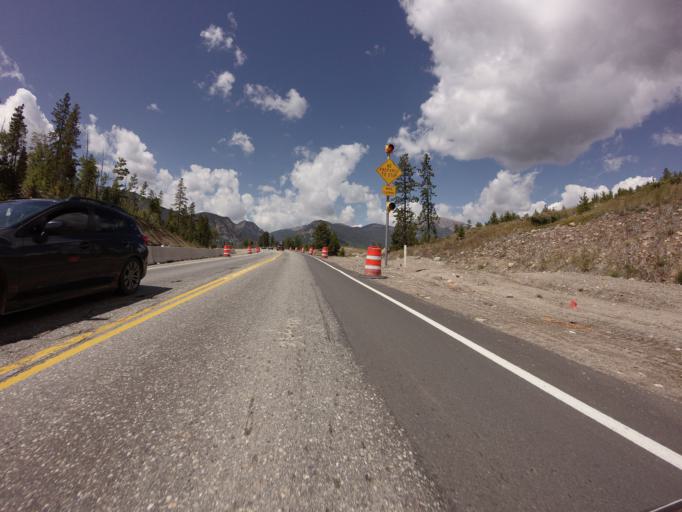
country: US
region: Colorado
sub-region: Summit County
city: Frisco
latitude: 39.5727
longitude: -106.0710
